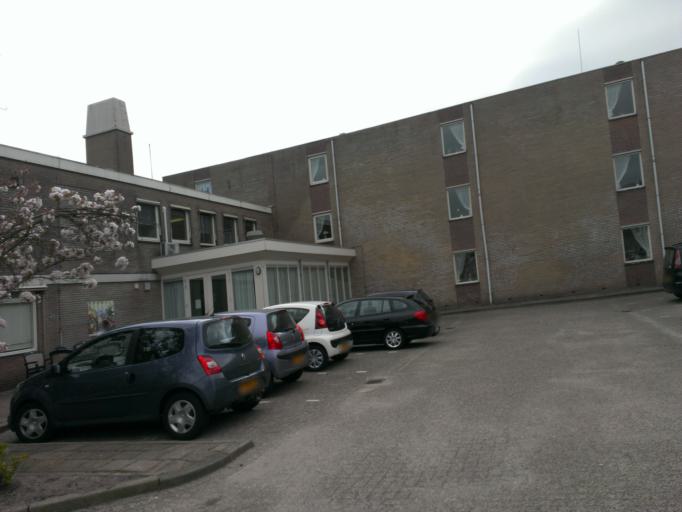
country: NL
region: Drenthe
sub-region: Gemeente Hoogeveen
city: Hoogeveen
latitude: 52.7268
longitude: 6.4686
